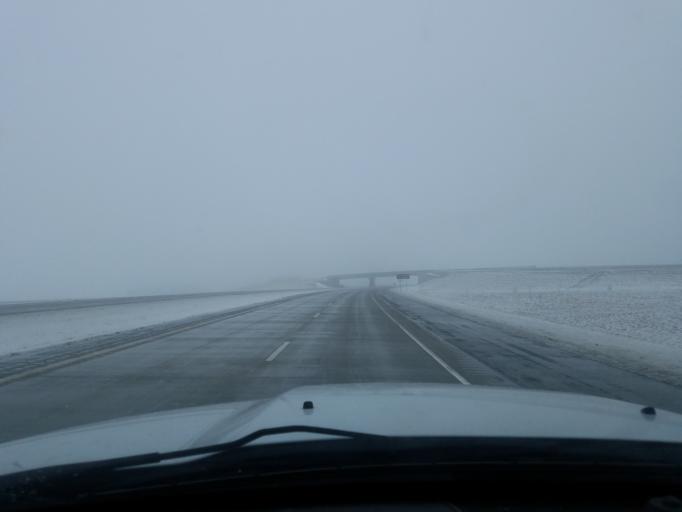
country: US
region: Indiana
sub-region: Howard County
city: Indian Heights
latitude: 40.3925
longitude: -86.1268
